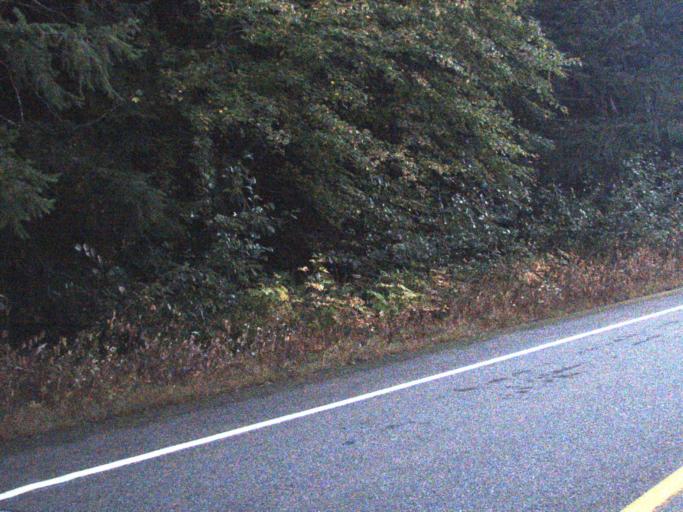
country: US
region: Washington
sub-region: Snohomish County
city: Darrington
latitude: 48.7096
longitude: -120.9841
